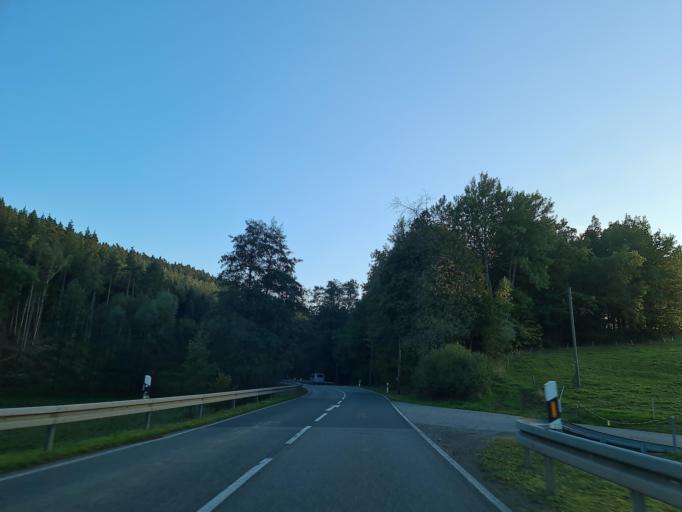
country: DE
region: Saxony
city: Elsterberg
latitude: 50.5881
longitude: 12.1376
